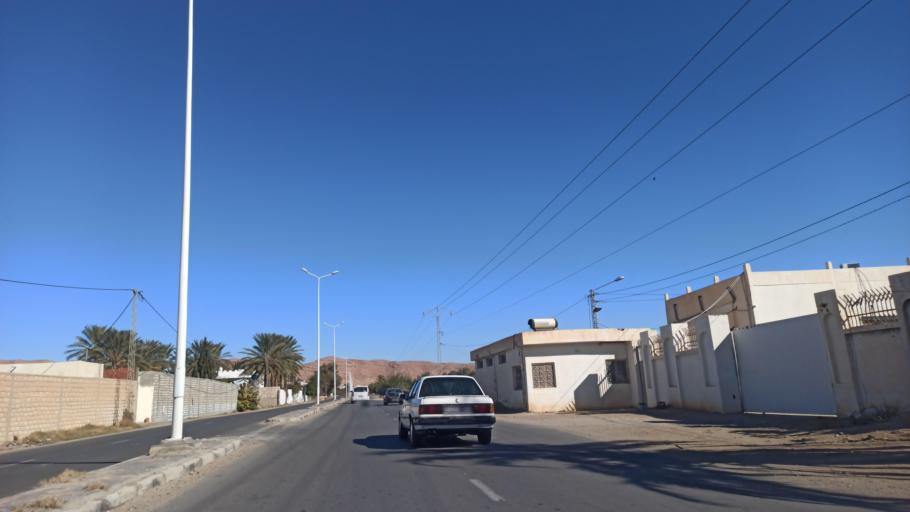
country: TN
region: Gafsa
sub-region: Gafsa Municipality
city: Gafsa
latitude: 34.4117
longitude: 8.7381
